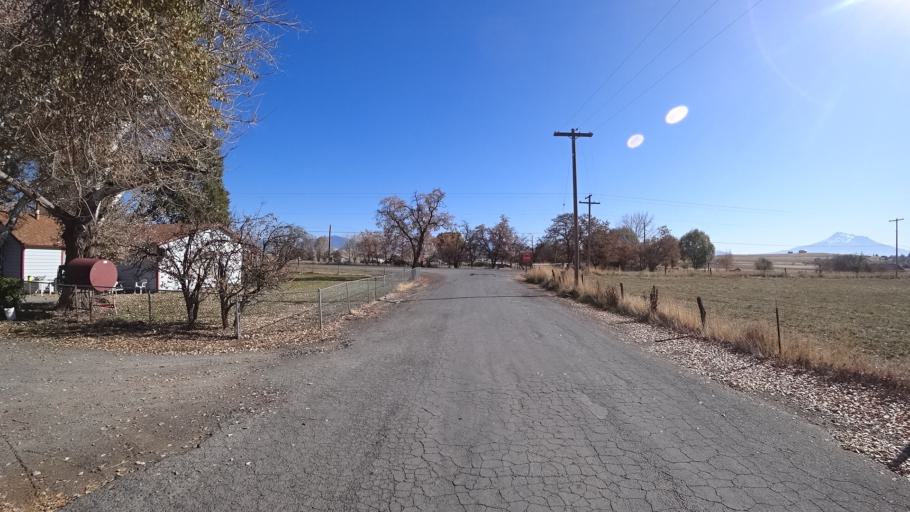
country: US
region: California
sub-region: Siskiyou County
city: Montague
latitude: 41.7420
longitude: -122.5252
